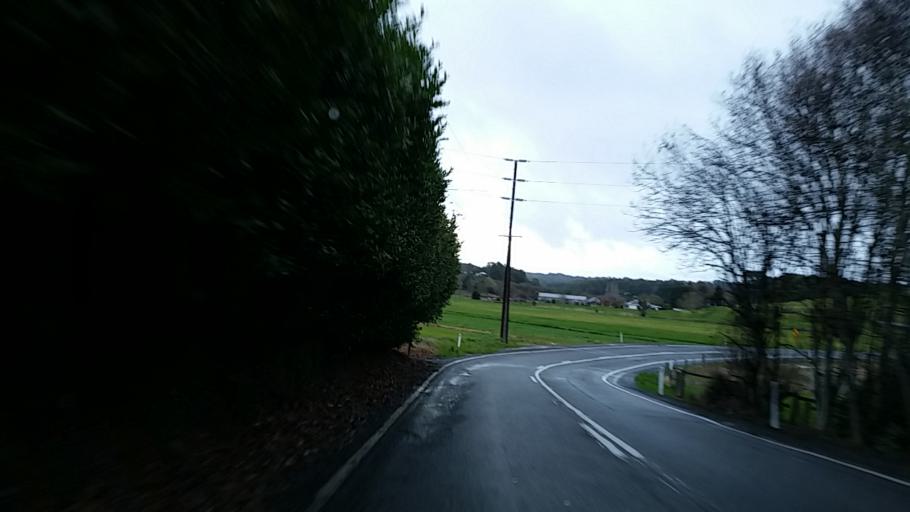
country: AU
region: South Australia
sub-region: Adelaide Hills
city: Bridgewater
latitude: -34.9651
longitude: 138.7348
